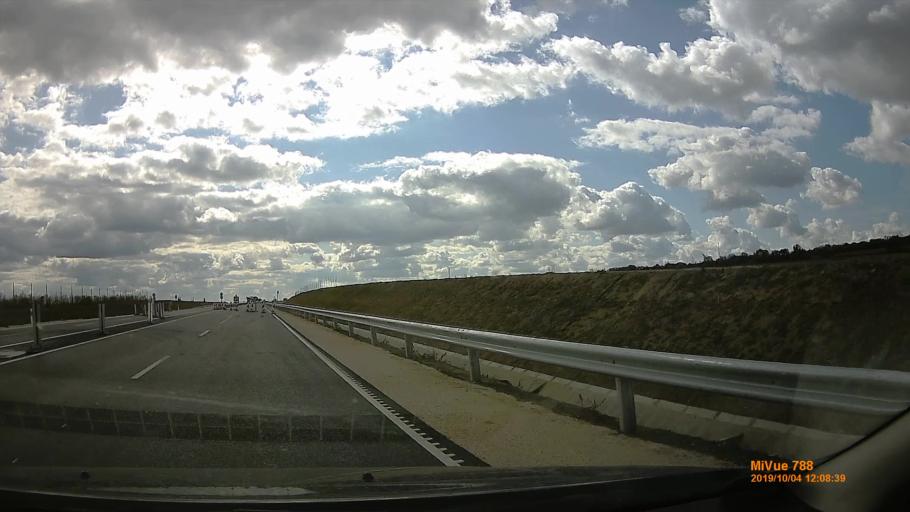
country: HU
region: Somogy
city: Kaposvar
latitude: 46.5256
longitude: 17.8182
